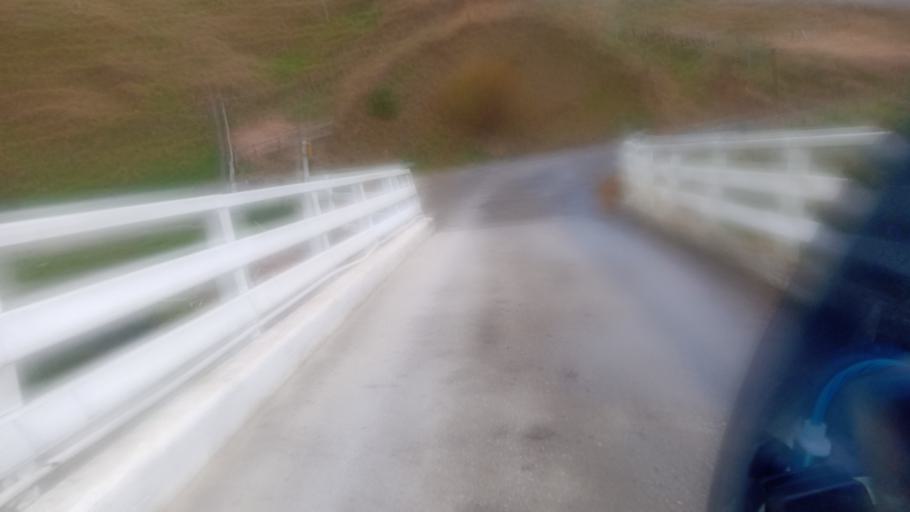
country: NZ
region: Gisborne
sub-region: Gisborne District
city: Gisborne
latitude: -38.5869
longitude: 178.1795
